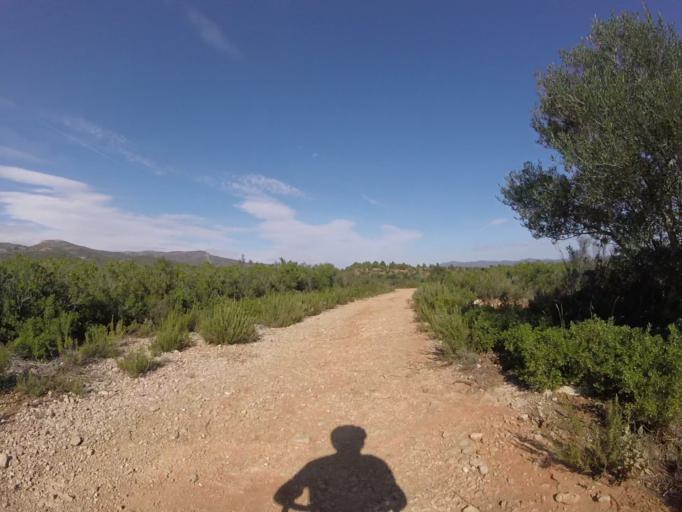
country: ES
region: Valencia
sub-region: Provincia de Castello
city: Cuevas de Vinroma
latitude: 40.2805
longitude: 0.0773
